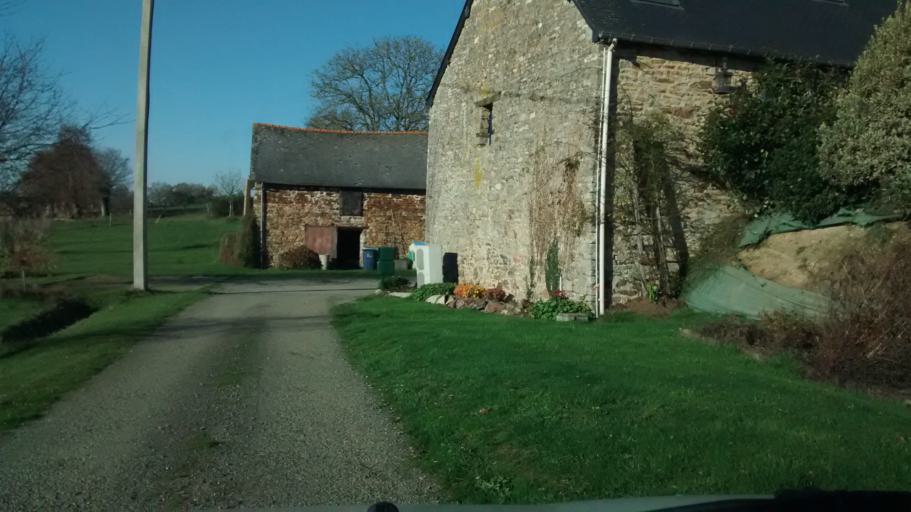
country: FR
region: Brittany
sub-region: Departement d'Ille-et-Vilaine
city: Gosne
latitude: 48.2085
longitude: -1.4691
